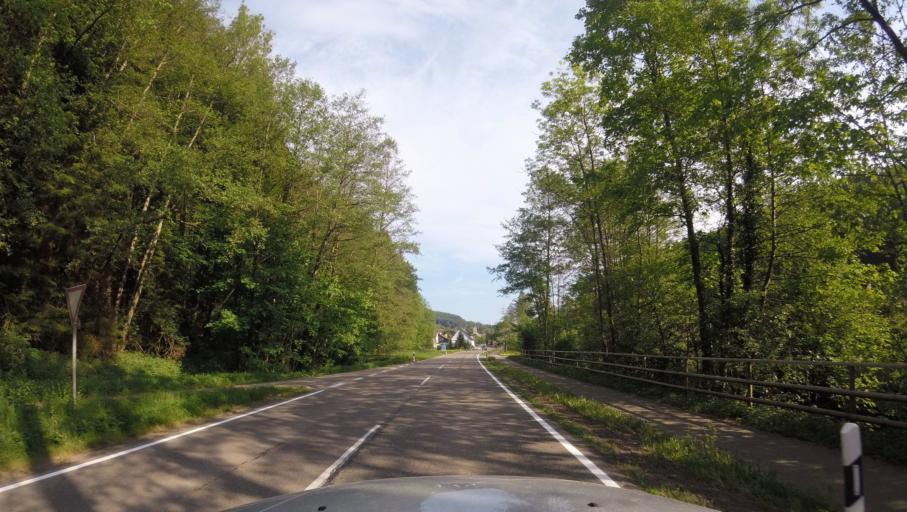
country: DE
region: Baden-Wuerttemberg
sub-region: Regierungsbezirk Stuttgart
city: Spiegelberg
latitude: 49.0321
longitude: 9.4486
